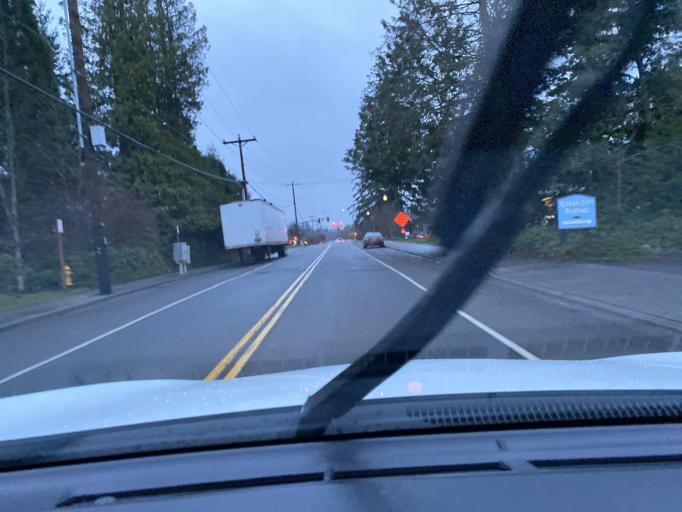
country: US
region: Washington
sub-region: Snohomish County
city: Mukilteo
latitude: 47.8902
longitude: -122.2891
